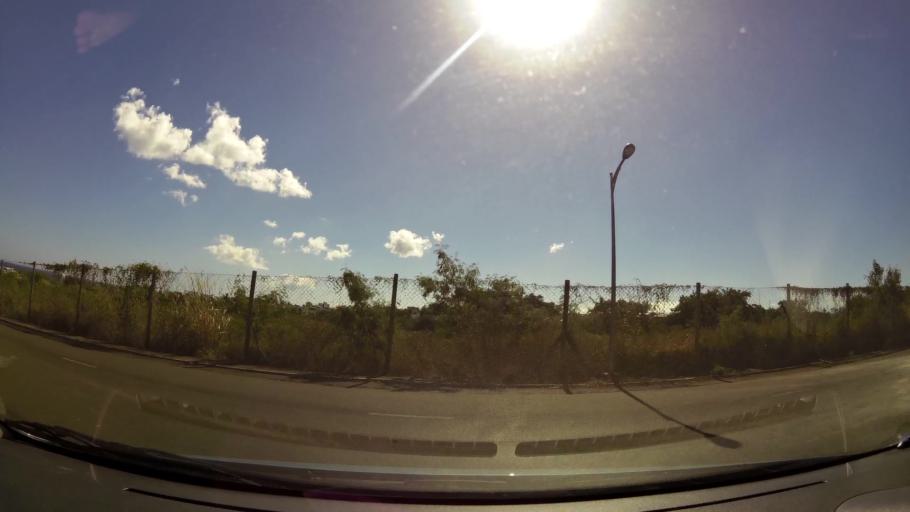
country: MU
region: Black River
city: Flic en Flac
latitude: -20.2823
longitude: 57.3779
